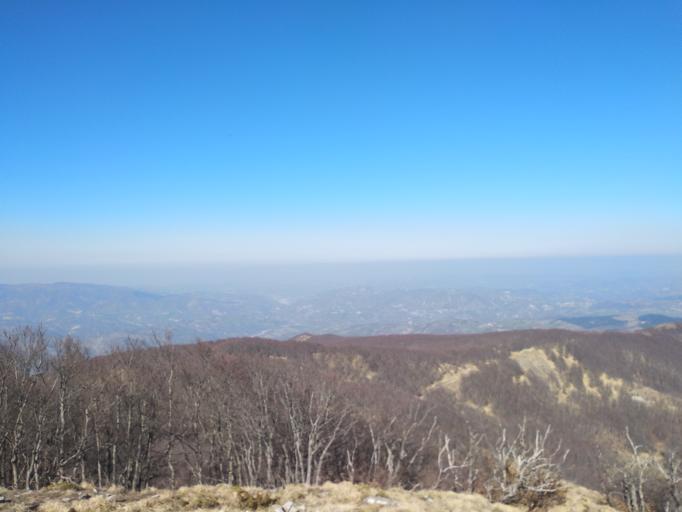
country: IT
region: Emilia-Romagna
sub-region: Provincia di Reggio Emilia
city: Busana
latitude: 44.3806
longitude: 10.2943
